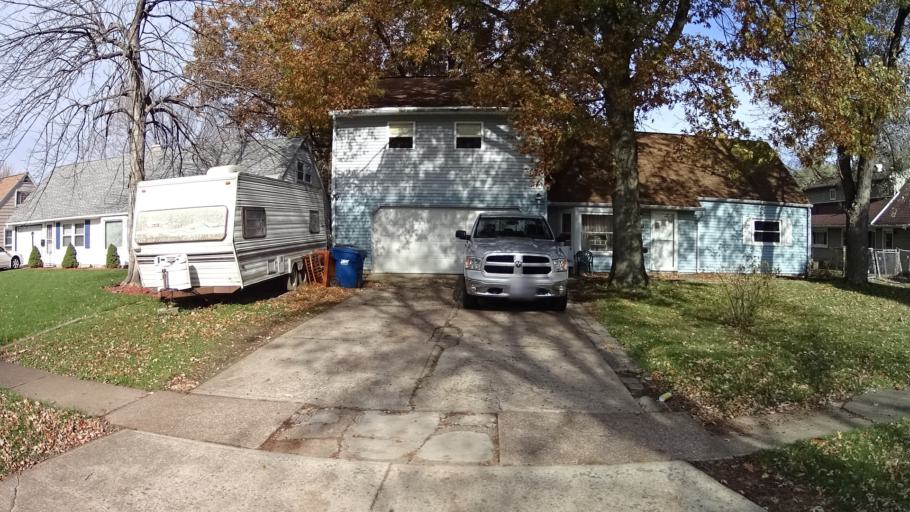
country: US
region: Ohio
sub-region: Lorain County
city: Sheffield Lake
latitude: 41.4863
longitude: -82.0875
